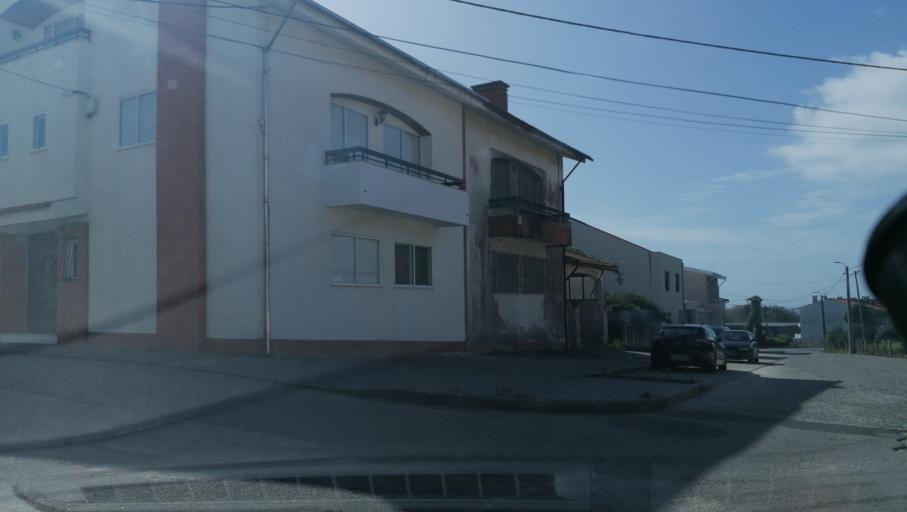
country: PT
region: Aveiro
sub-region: Espinho
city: Espinho
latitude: 41.0152
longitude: -8.6361
